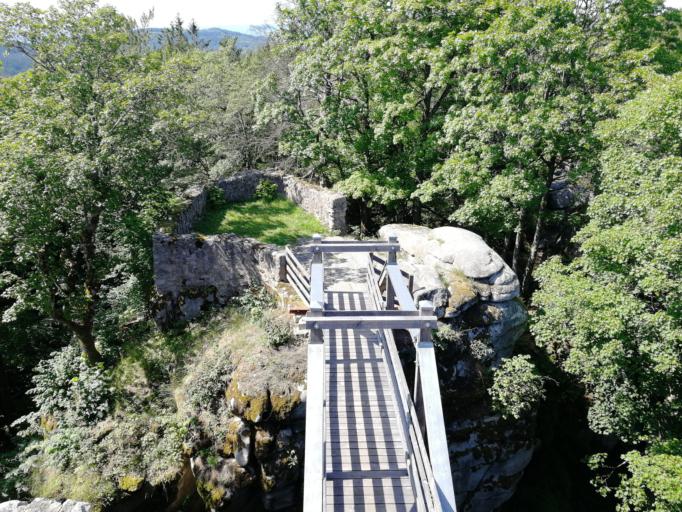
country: DE
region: Bavaria
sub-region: Upper Palatinate
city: Georgenberg
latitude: 49.7322
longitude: 12.3989
